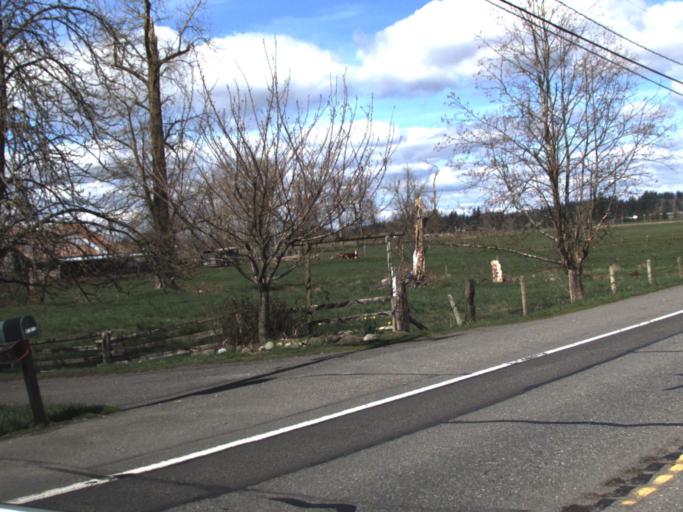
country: US
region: Washington
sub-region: King County
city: Enumclaw
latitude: 47.2256
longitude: -121.9897
